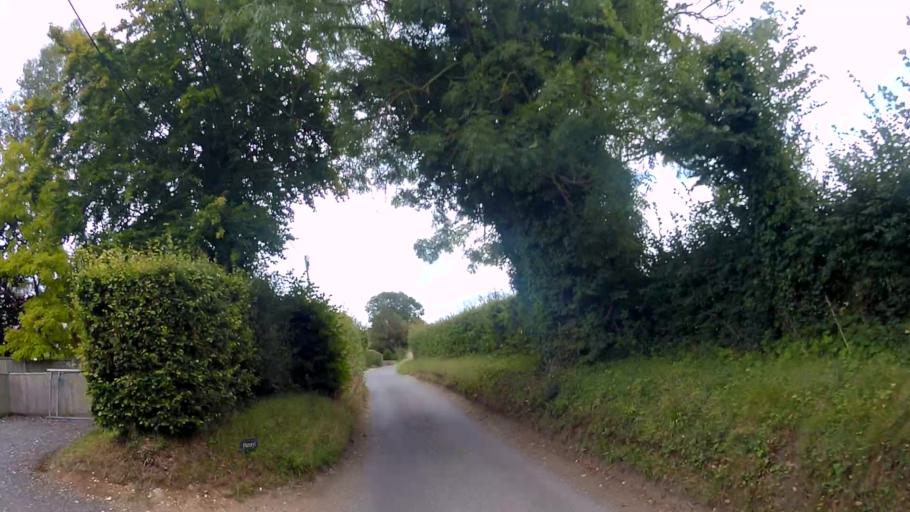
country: GB
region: England
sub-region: Hampshire
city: Kings Worthy
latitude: 51.1678
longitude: -1.3339
